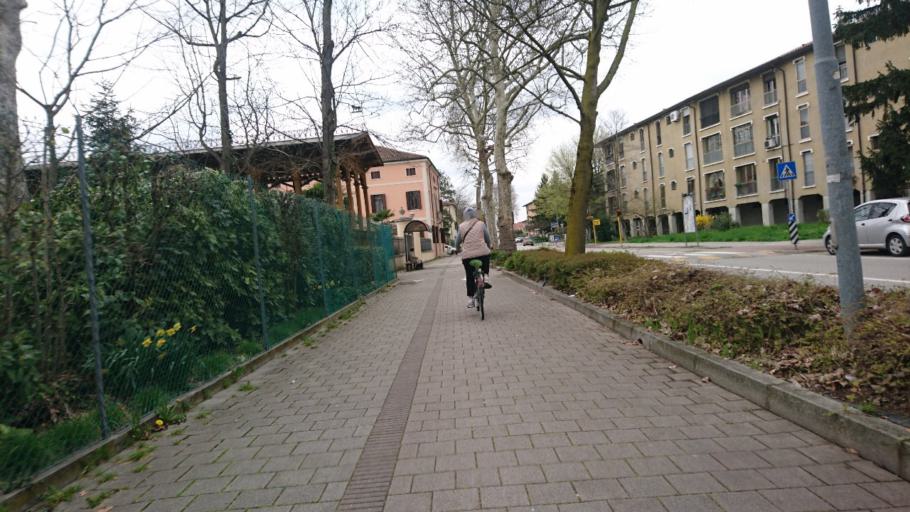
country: IT
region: Veneto
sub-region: Provincia di Padova
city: Vigodarzere
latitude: 45.4370
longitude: 11.8702
